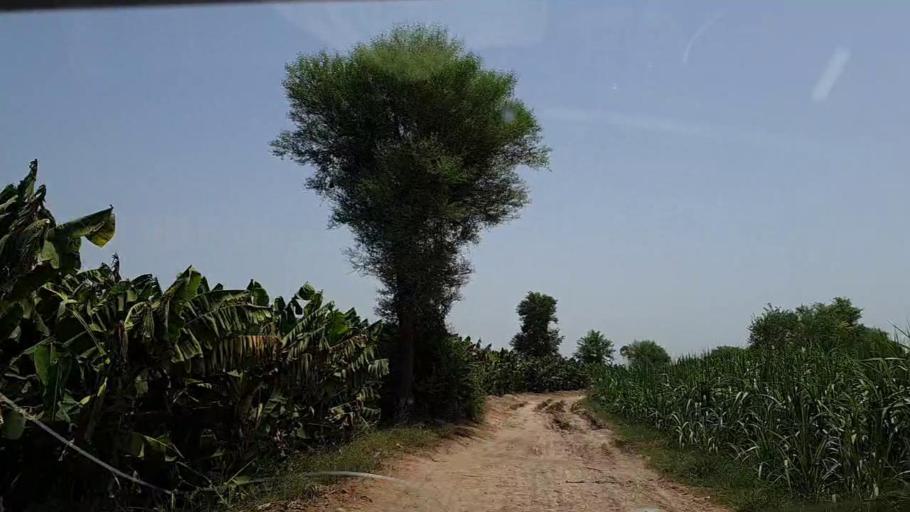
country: PK
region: Sindh
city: Tharu Shah
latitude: 26.9321
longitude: 68.0399
